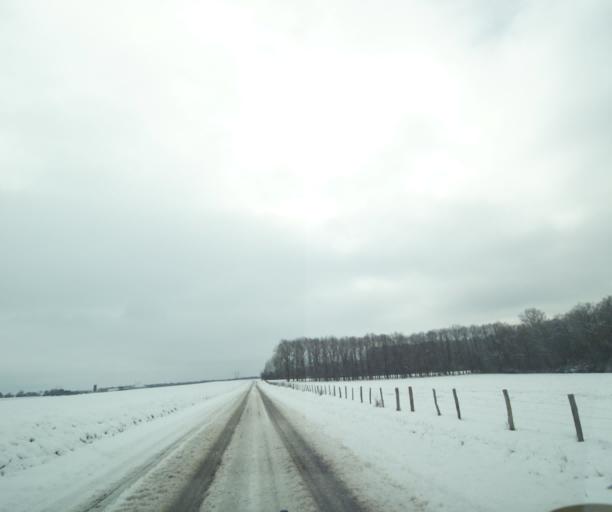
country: FR
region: Champagne-Ardenne
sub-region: Departement de la Haute-Marne
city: Montier-en-Der
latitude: 48.5181
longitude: 4.6791
